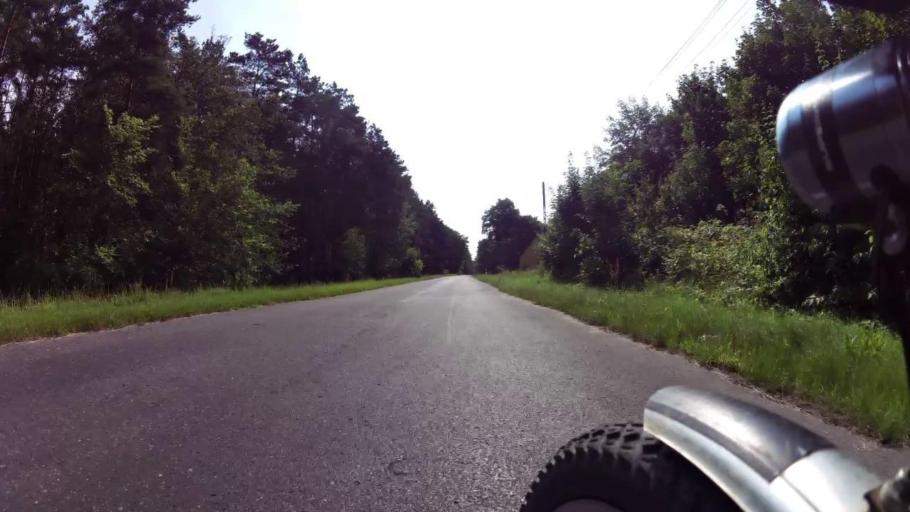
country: DE
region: Brandenburg
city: Zechin
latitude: 52.6779
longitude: 14.4879
